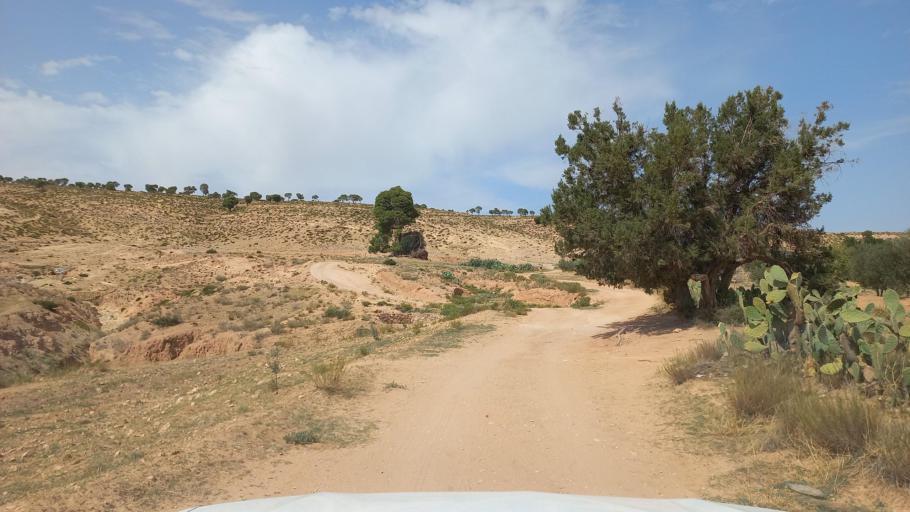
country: TN
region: Al Qasrayn
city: Kasserine
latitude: 35.3715
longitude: 8.8792
